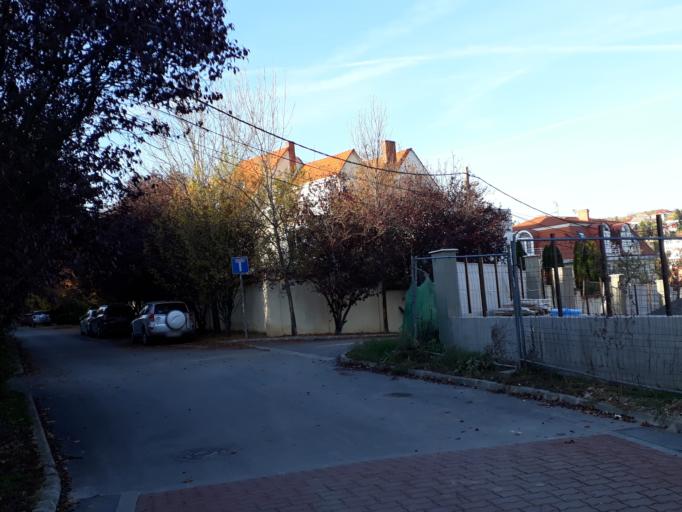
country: HU
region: Budapest
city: Budapest XII. keruelet
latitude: 47.4756
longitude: 18.9949
